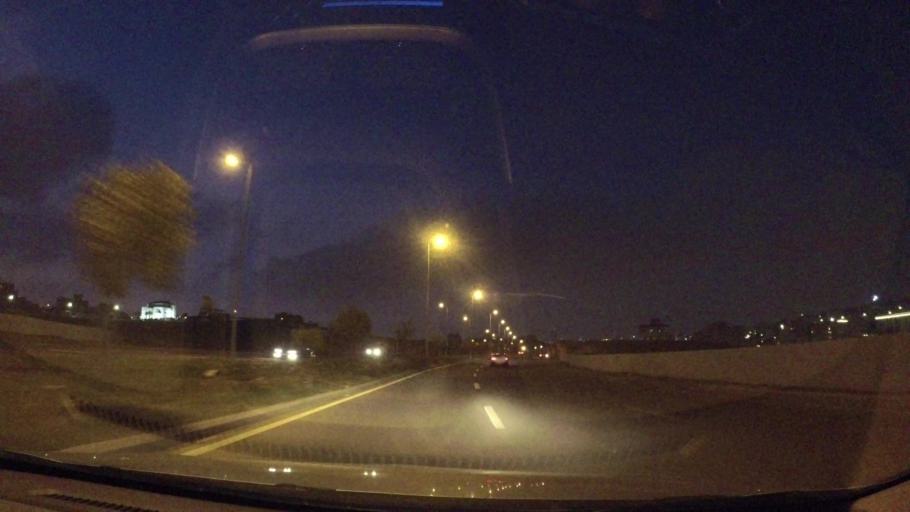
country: JO
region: Amman
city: Al Bunayyat ash Shamaliyah
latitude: 31.9120
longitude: 35.8800
